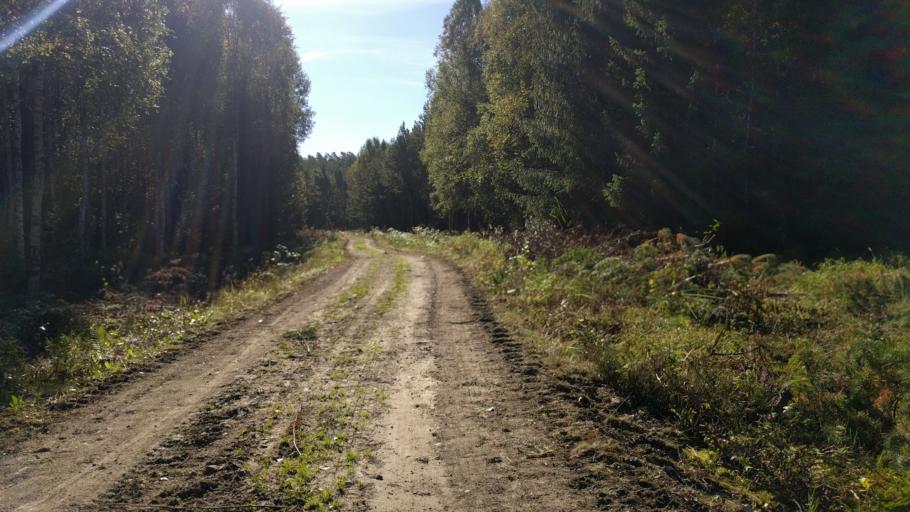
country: SE
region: Stockholm
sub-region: Vallentuna Kommun
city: Vallentuna
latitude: 59.4948
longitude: 18.1113
